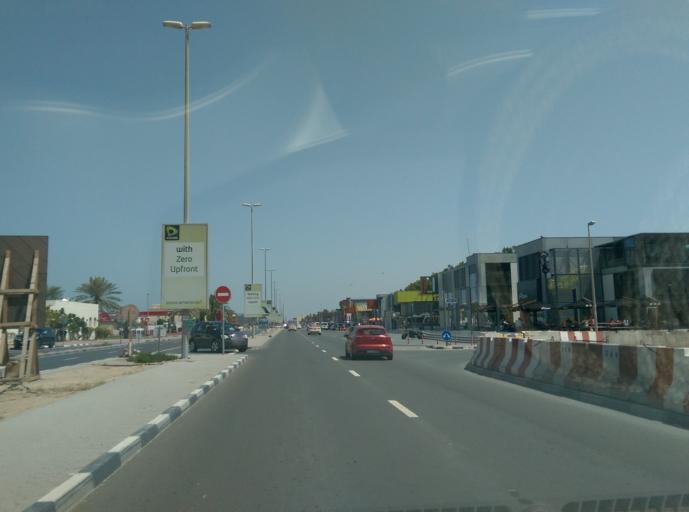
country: AE
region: Dubai
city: Dubai
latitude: 25.1959
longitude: 55.2461
